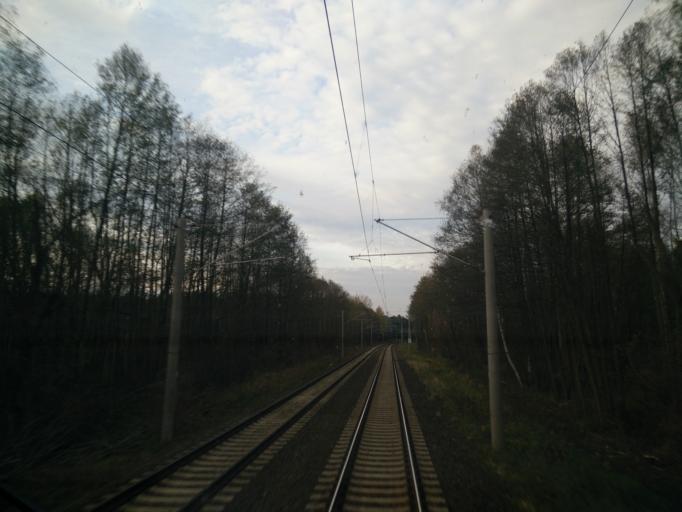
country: DE
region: Brandenburg
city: Bestensee
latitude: 52.2081
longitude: 13.6203
